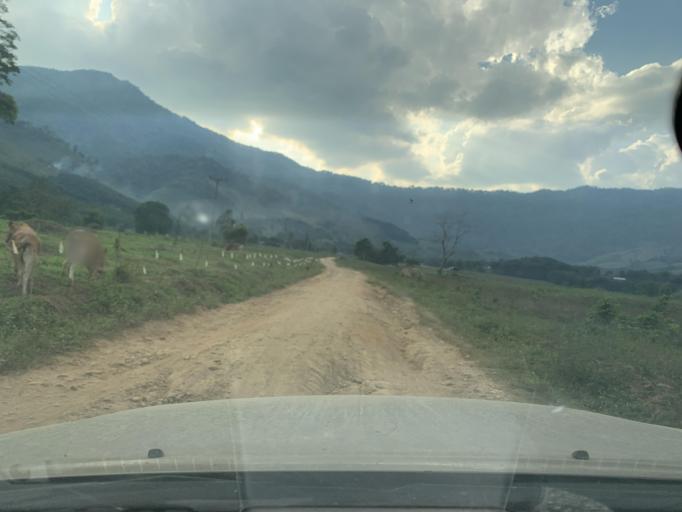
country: TH
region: Phayao
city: Phu Sang
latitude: 19.7424
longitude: 100.4379
